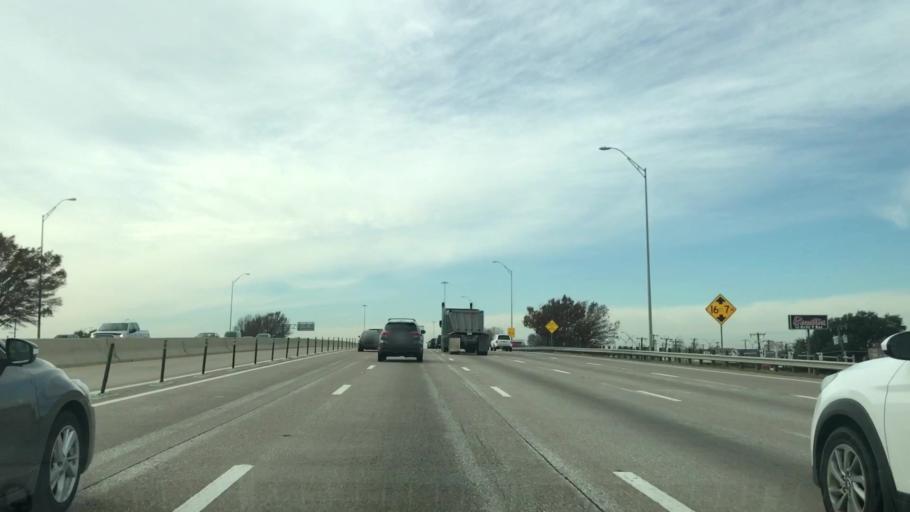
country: US
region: Texas
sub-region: Dallas County
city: Richardson
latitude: 32.9412
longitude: -96.7444
